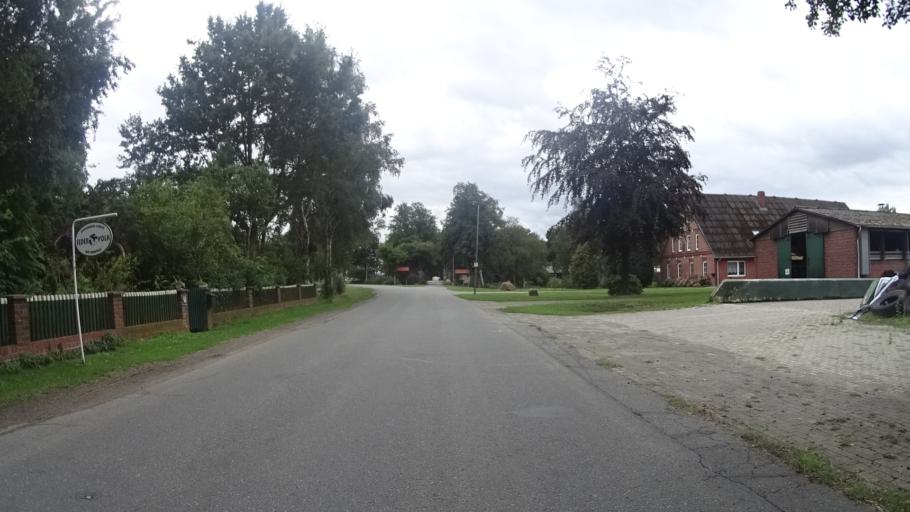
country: DE
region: Lower Saxony
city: Stinstedt
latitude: 53.6420
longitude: 8.9445
